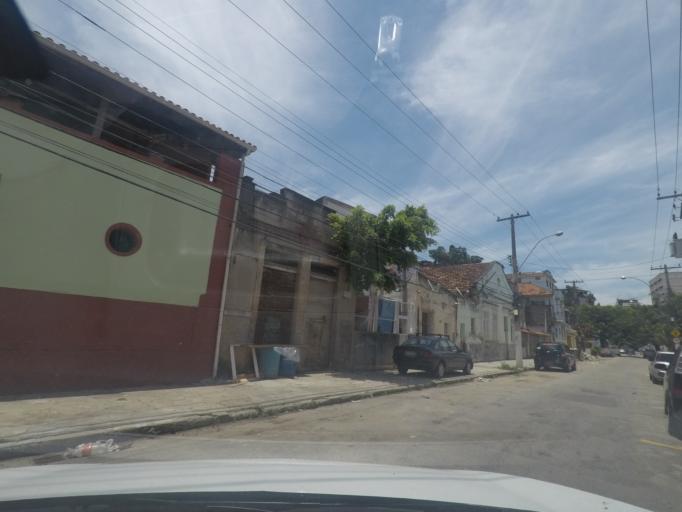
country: BR
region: Rio de Janeiro
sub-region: Niteroi
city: Niteroi
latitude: -22.8965
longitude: -43.1196
